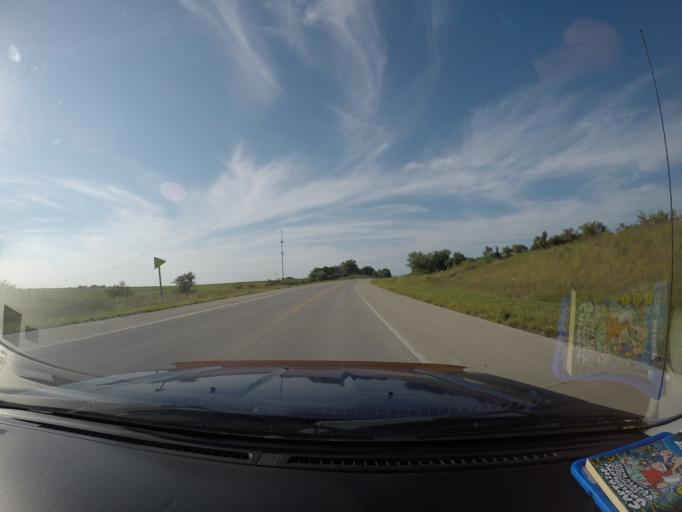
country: US
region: Kansas
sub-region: Leavenworth County
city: Leavenworth
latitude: 39.3778
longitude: -95.0567
